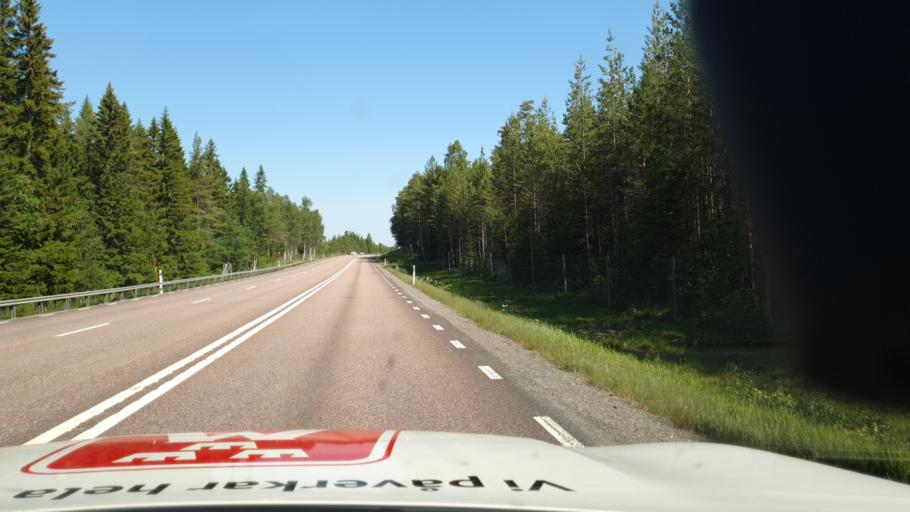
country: SE
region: Vaesterbotten
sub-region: Skelleftea Kommun
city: Burea
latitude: 64.4484
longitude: 21.2838
